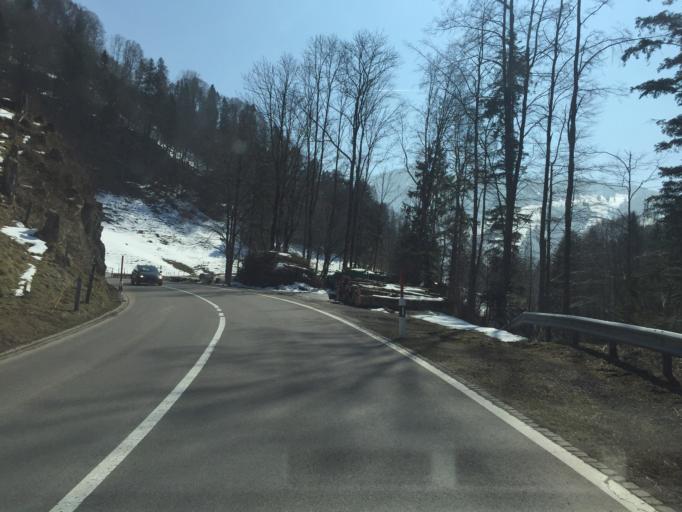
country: CH
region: Saint Gallen
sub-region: Wahlkreis Toggenburg
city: Krummenau
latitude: 47.2123
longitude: 9.2168
